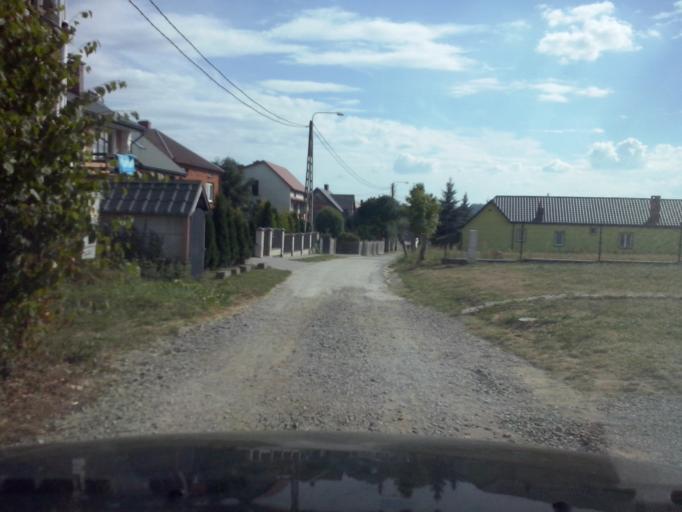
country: PL
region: Swietokrzyskie
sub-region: Powiat kielecki
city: Lagow
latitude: 50.7824
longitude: 21.0875
